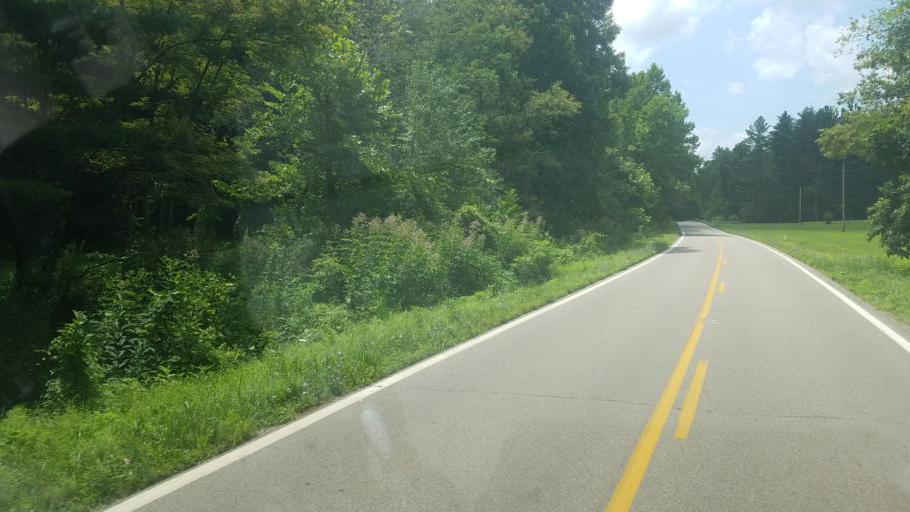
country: US
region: Ohio
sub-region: Ross County
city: Kingston
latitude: 39.3828
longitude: -82.7272
